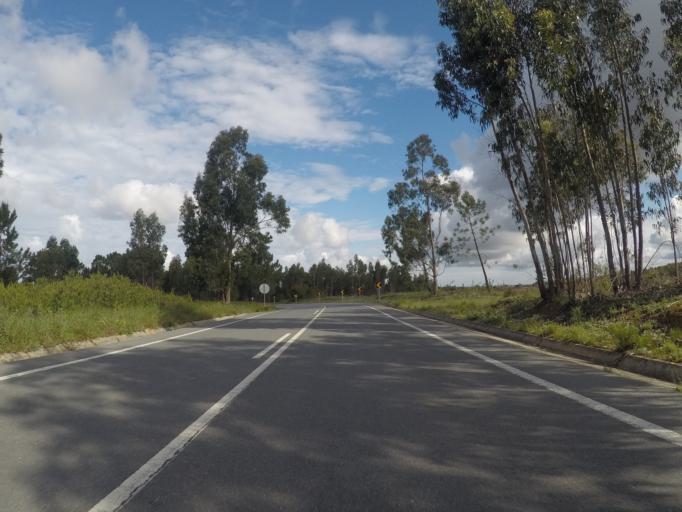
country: PT
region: Faro
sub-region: Aljezur
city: Aljezur
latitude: 37.2405
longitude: -8.8017
